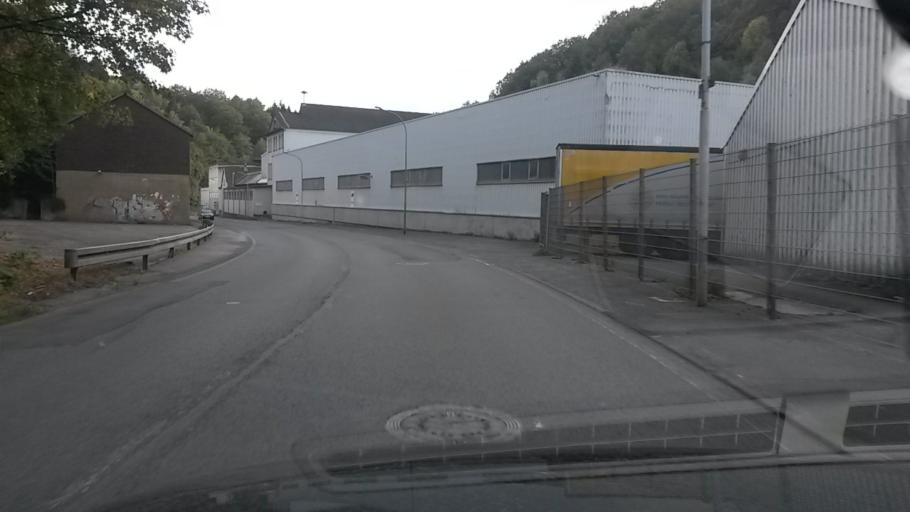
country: DE
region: North Rhine-Westphalia
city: Werdohl
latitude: 51.2342
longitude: 7.7236
